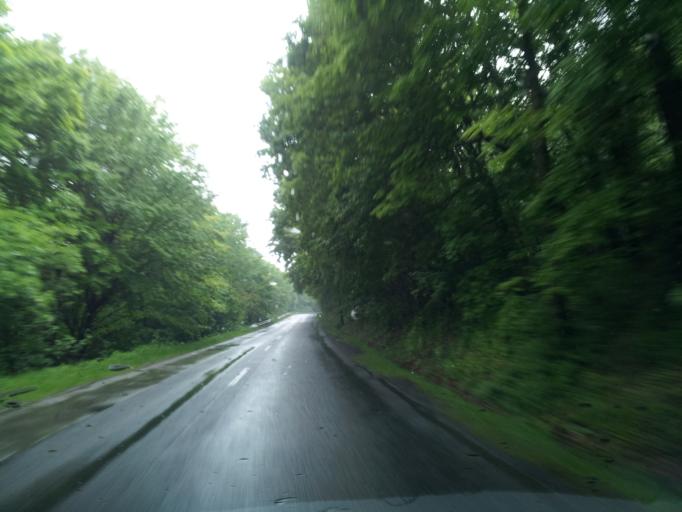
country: HU
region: Baranya
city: Hosszuheteny
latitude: 46.1773
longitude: 18.3212
